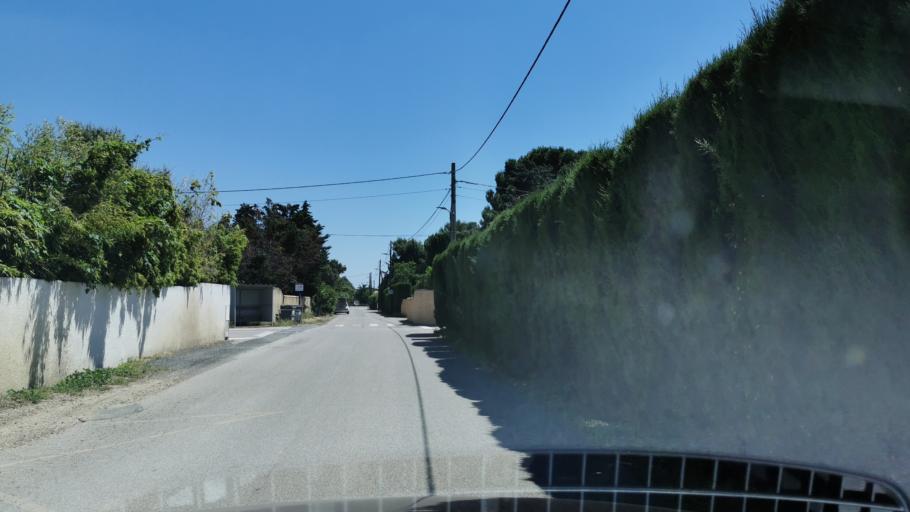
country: FR
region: Languedoc-Roussillon
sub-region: Departement de l'Aude
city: Ouveillan
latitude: 43.2605
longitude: 3.0094
